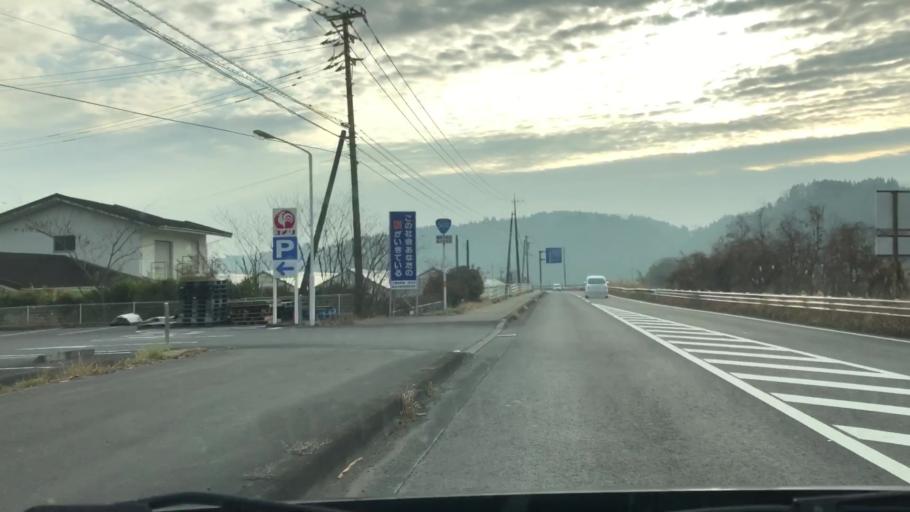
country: JP
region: Oita
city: Takedamachi
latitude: 32.9659
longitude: 131.4818
